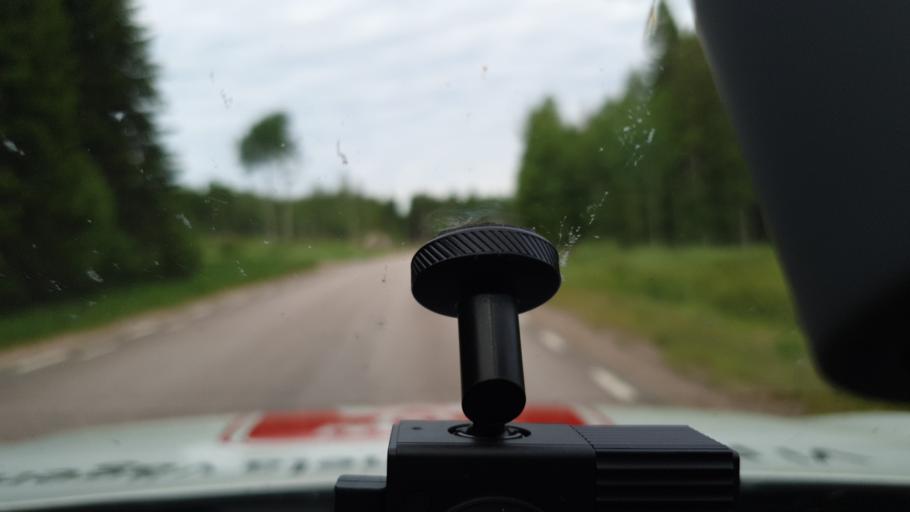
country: SE
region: Vaermland
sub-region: Torsby Kommun
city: Torsby
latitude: 60.1213
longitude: 12.9517
